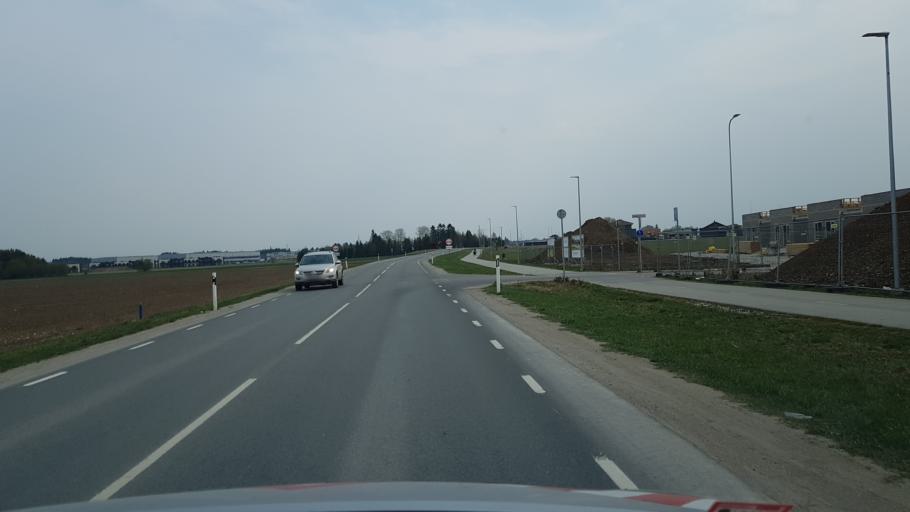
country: EE
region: Harju
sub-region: Tallinna linn
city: Tallinn
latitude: 59.3874
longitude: 24.8115
